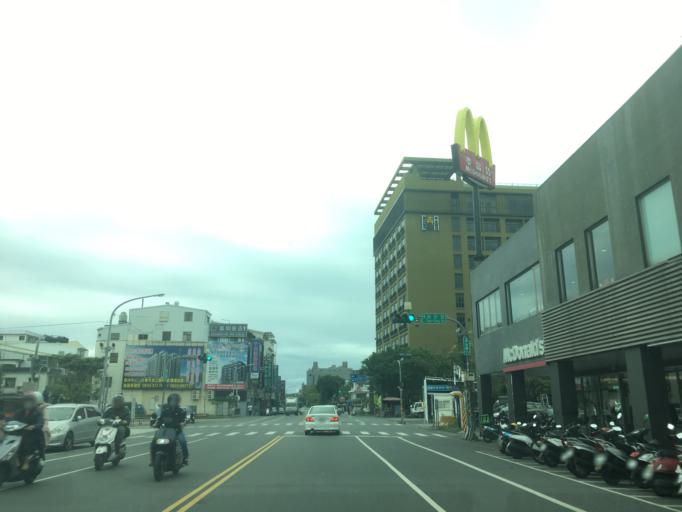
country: TW
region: Taiwan
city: Taitung City
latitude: 22.7556
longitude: 121.1447
